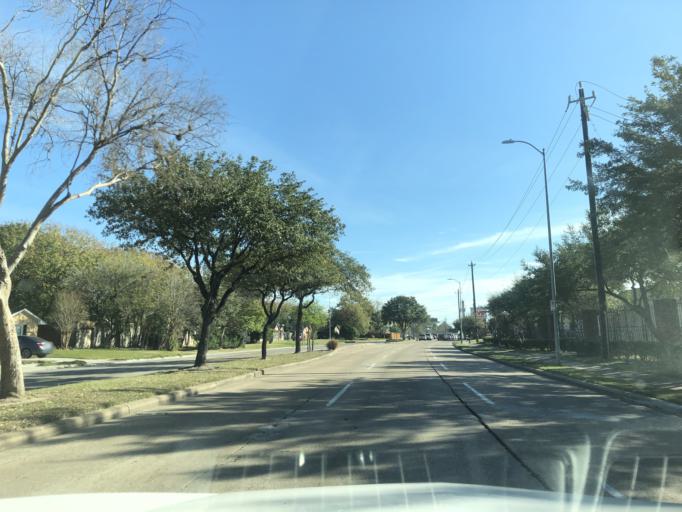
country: US
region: Texas
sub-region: Harris County
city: Bellaire
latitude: 29.6942
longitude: -95.5112
